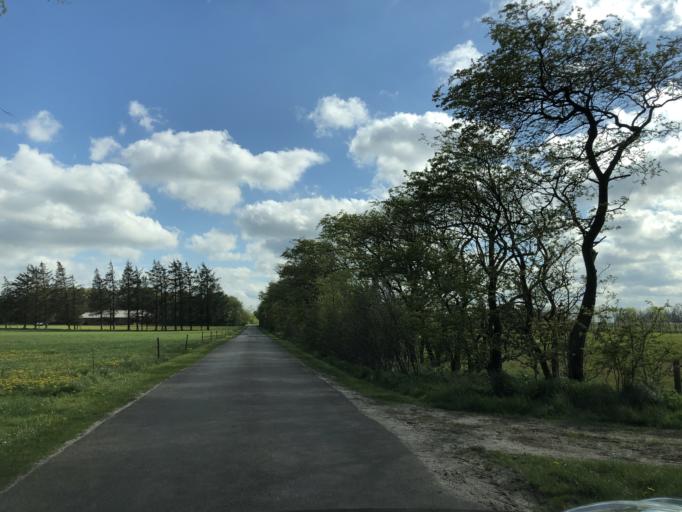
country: DK
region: Central Jutland
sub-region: Herning Kommune
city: Avlum
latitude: 56.2925
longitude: 8.7378
